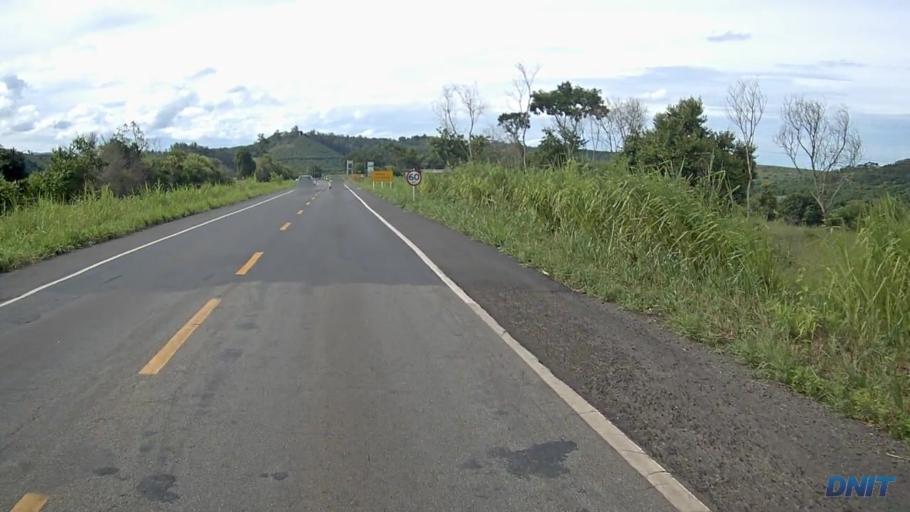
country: BR
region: Minas Gerais
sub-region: Ipaba
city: Ipaba
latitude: -19.2894
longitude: -42.3561
